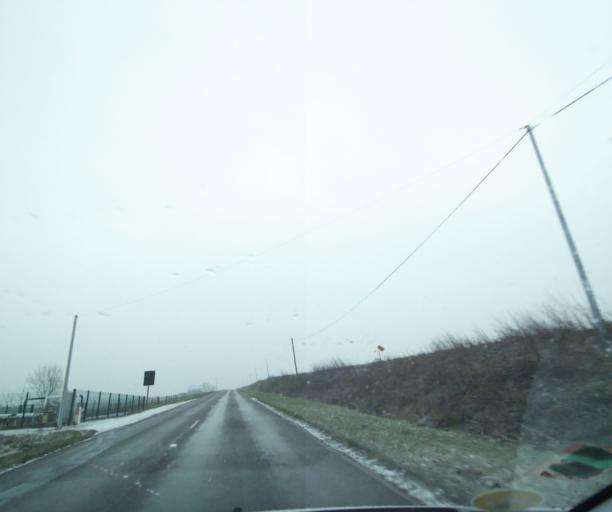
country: FR
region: Champagne-Ardenne
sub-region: Departement de la Haute-Marne
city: Wassy
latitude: 48.4882
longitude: 4.9753
